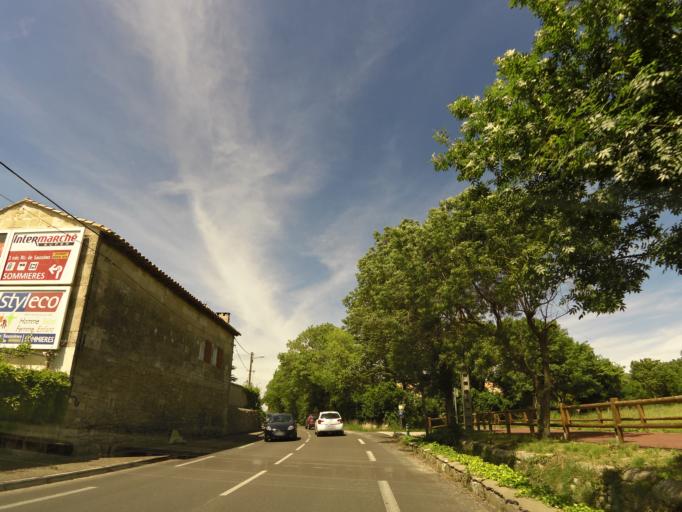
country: FR
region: Languedoc-Roussillon
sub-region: Departement du Gard
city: Sommieres
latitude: 43.7920
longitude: 4.0885
